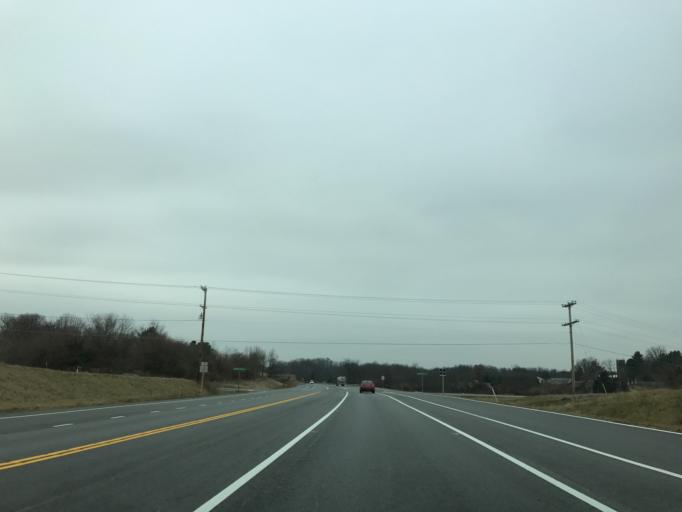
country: US
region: Maryland
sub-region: Carroll County
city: Westminster
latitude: 39.6067
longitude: -77.0617
